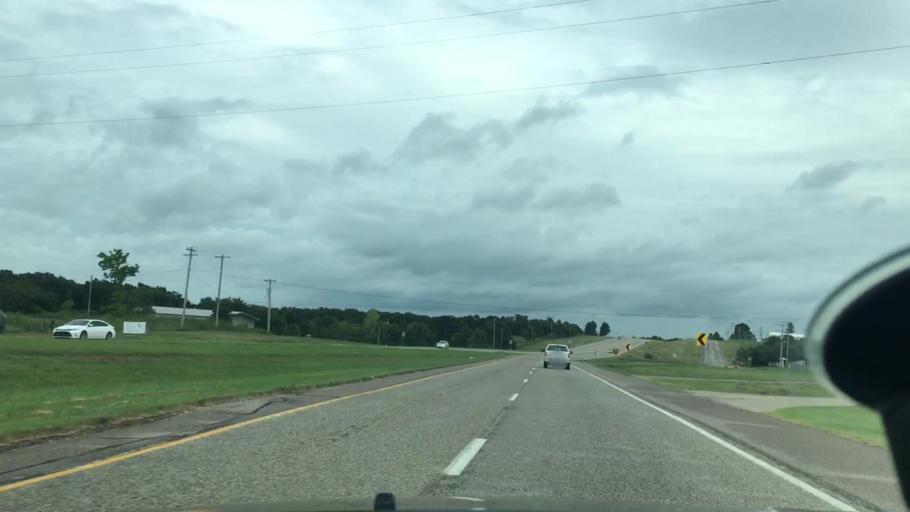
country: US
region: Oklahoma
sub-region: Seminole County
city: Seminole
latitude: 35.2790
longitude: -96.6711
